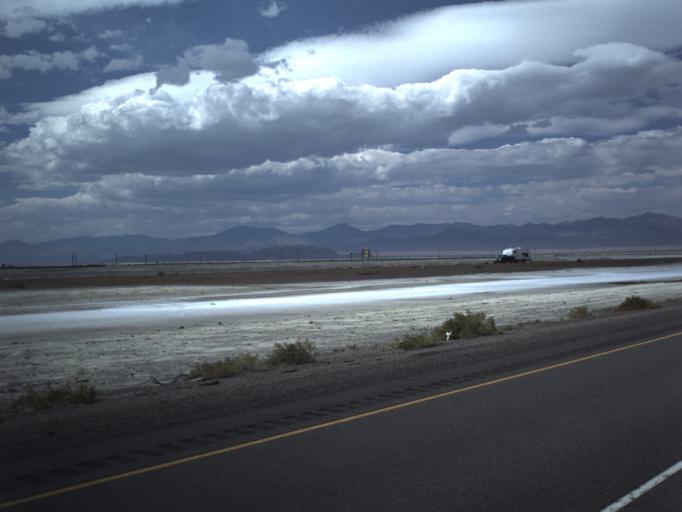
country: US
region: Utah
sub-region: Tooele County
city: Wendover
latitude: 40.7412
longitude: -113.9441
